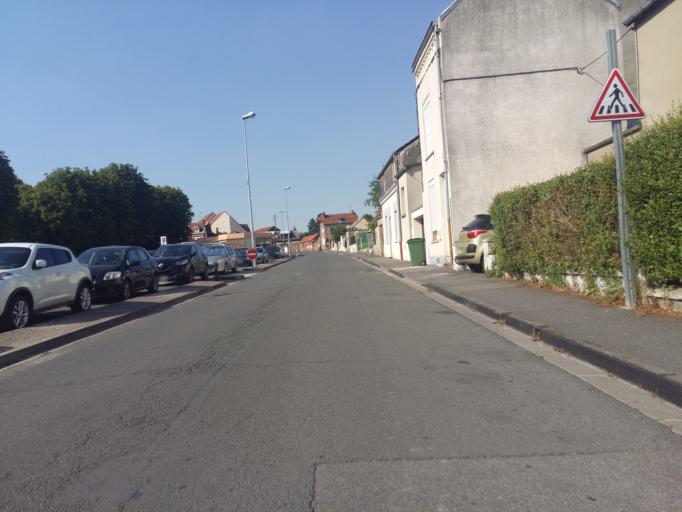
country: FR
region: Picardie
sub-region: Departement de la Somme
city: Rivery
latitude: 49.9010
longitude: 2.3224
